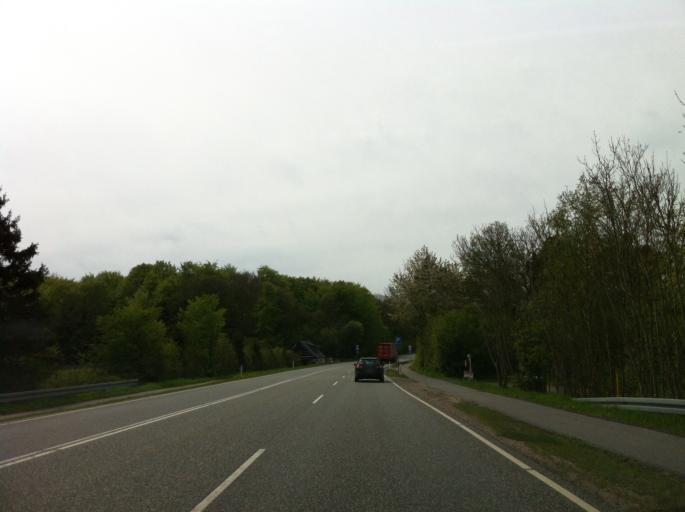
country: DK
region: Zealand
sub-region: Lejre Kommune
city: Osted
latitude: 55.5154
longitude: 11.8965
